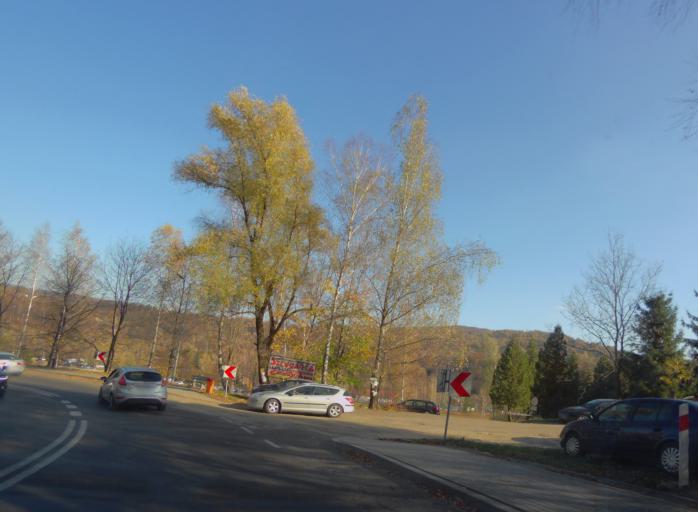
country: PL
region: Subcarpathian Voivodeship
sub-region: Powiat leski
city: Polanczyk
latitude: 49.3994
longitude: 22.4511
